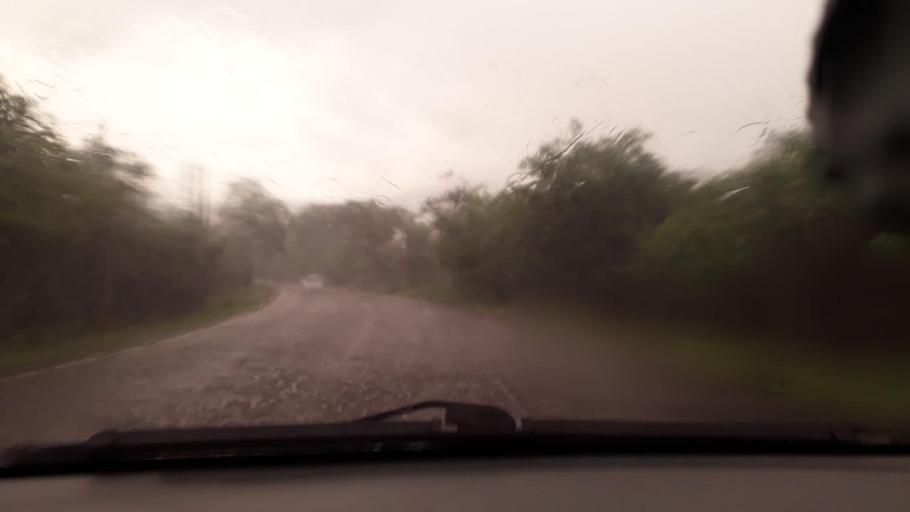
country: GT
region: Jutiapa
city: Comapa
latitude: 14.0386
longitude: -89.9151
